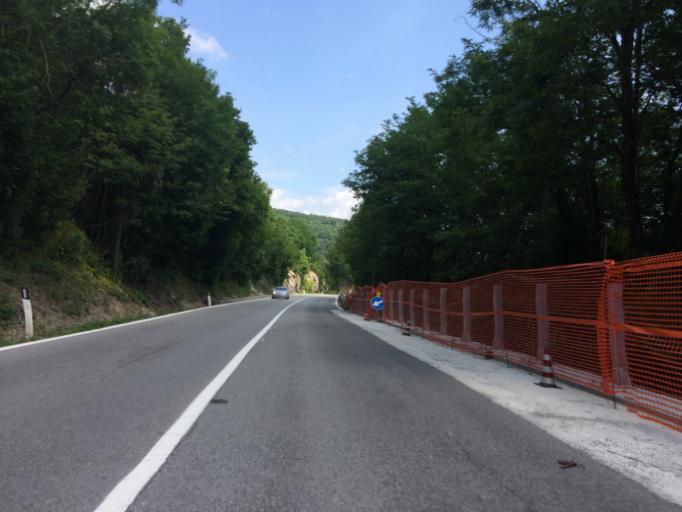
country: IT
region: Piedmont
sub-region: Provincia di Cuneo
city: Bagnasco
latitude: 44.2867
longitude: 8.0331
